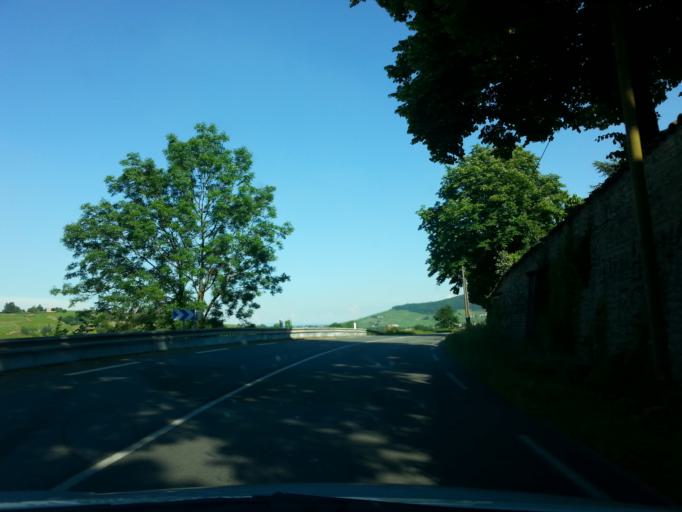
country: FR
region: Rhone-Alpes
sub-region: Departement du Rhone
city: Quincie-en-Beaujolais
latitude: 46.1370
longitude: 4.6128
